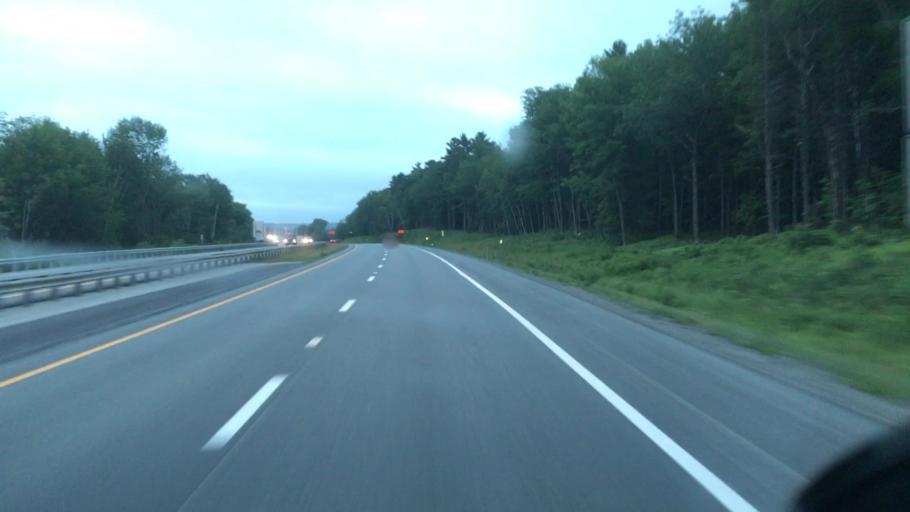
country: US
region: Maine
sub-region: Androscoggin County
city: Lewiston
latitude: 44.0686
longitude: -70.1723
